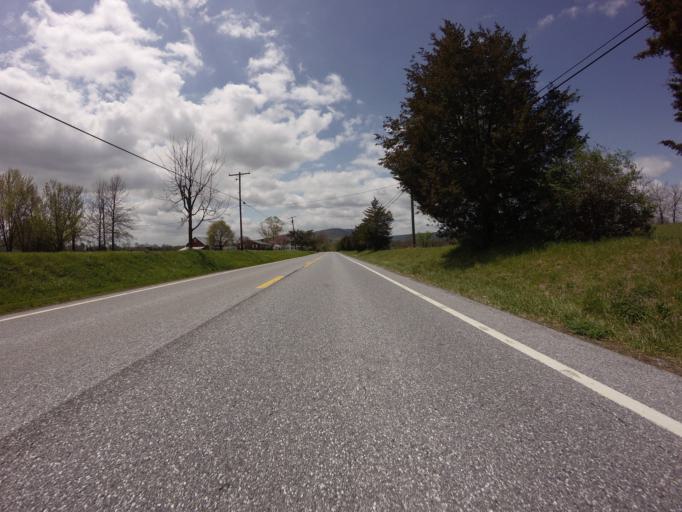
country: US
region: Maryland
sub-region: Frederick County
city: Emmitsburg
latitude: 39.7110
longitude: -77.3153
